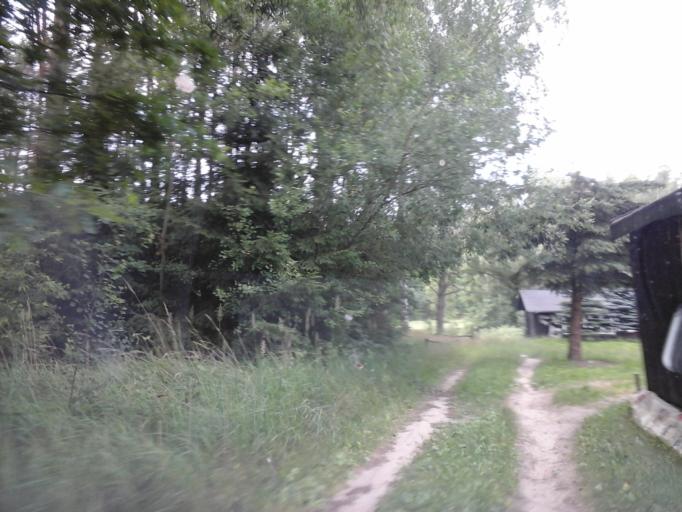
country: PL
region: Lubusz
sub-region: Powiat strzelecko-drezdenecki
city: Dobiegniew
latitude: 53.0691
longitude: 15.7728
